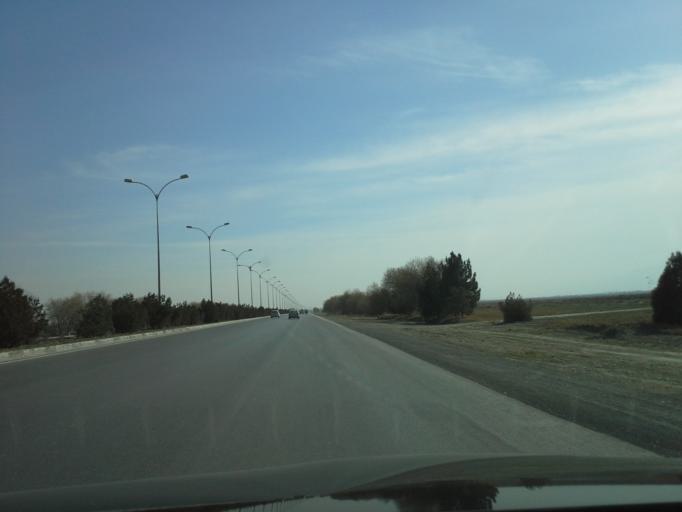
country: TM
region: Ahal
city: Abadan
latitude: 38.1323
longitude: 58.0196
